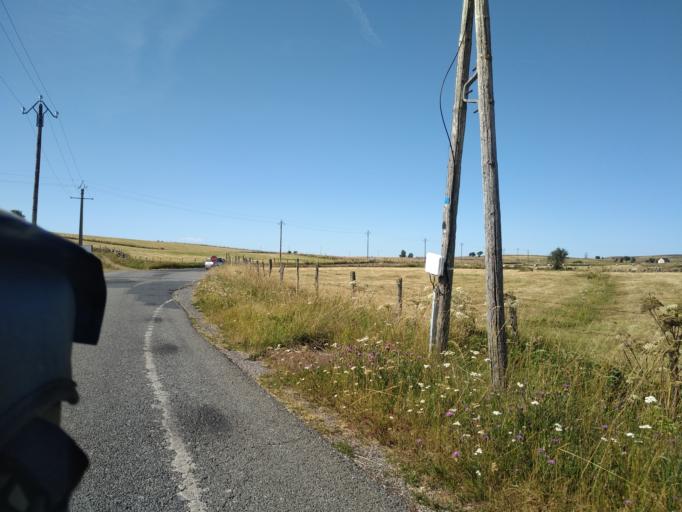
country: FR
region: Auvergne
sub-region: Departement du Cantal
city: Chaudes-Aigues
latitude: 44.6841
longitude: 3.0829
